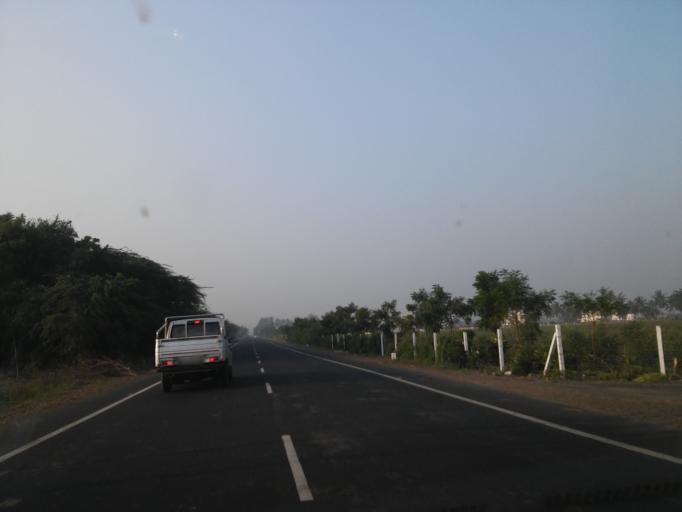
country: IN
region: Gujarat
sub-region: Kachchh
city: Mandvi
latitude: 22.8685
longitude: 69.3918
